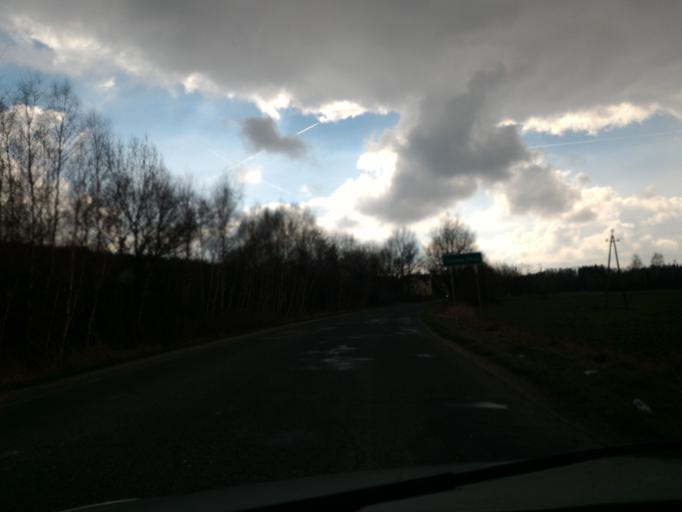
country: PL
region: Lower Silesian Voivodeship
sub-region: Powiat zgorzelecki
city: Bogatynia
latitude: 50.8842
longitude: 14.9398
